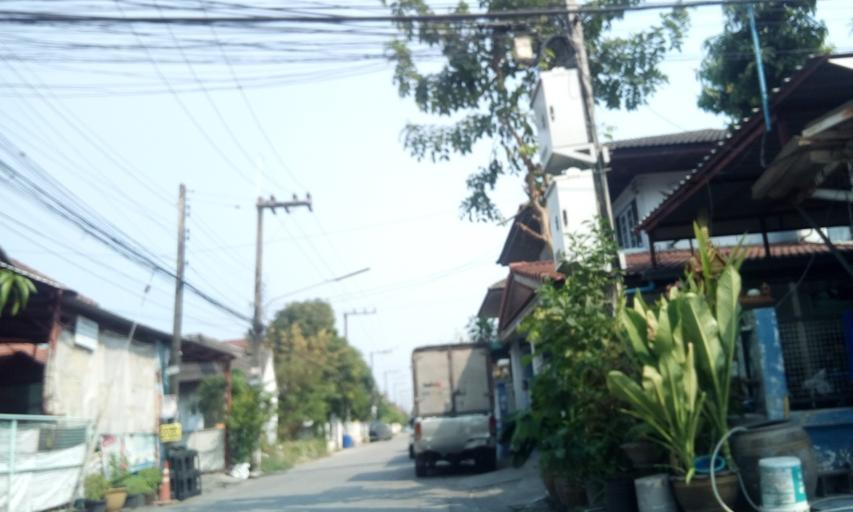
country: TH
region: Pathum Thani
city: Lam Luk Ka
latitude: 13.9361
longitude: 100.7203
